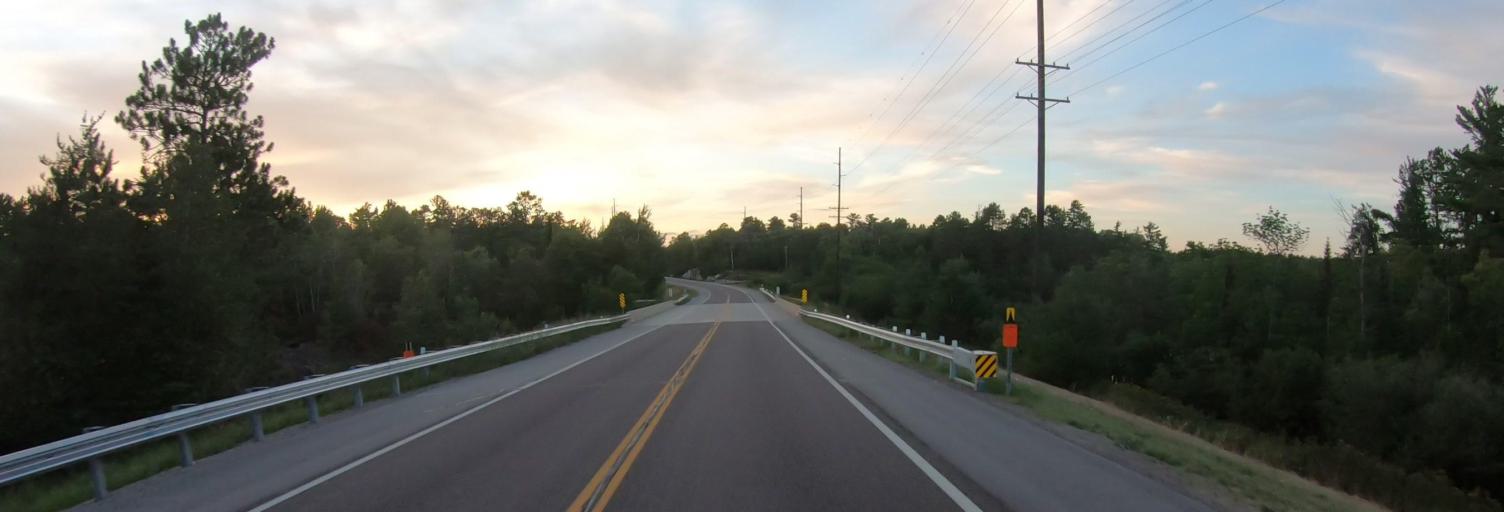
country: US
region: Minnesota
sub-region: Saint Louis County
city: Aurora
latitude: 47.7911
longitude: -92.3677
